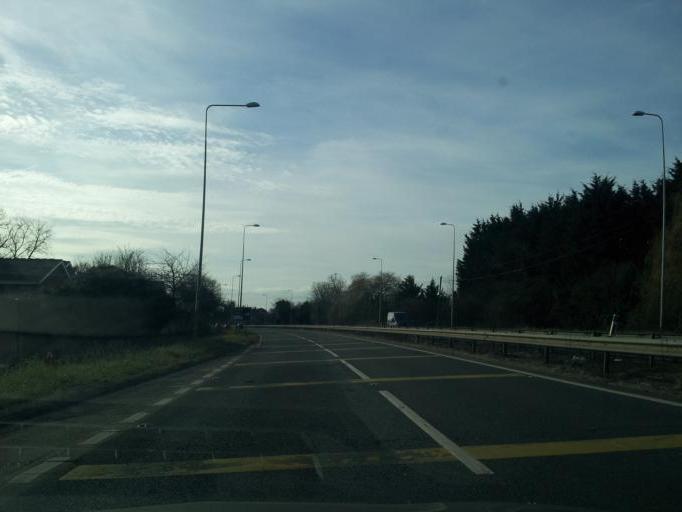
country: GB
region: England
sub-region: Central Bedfordshire
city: Sandy
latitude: 52.1317
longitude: -0.3007
